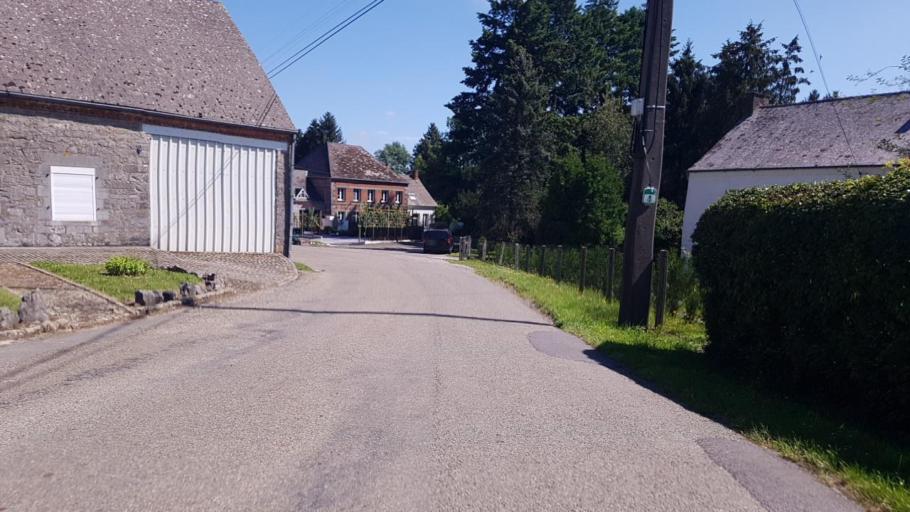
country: BE
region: Wallonia
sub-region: Province du Hainaut
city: Momignies
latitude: 50.0426
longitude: 4.2060
